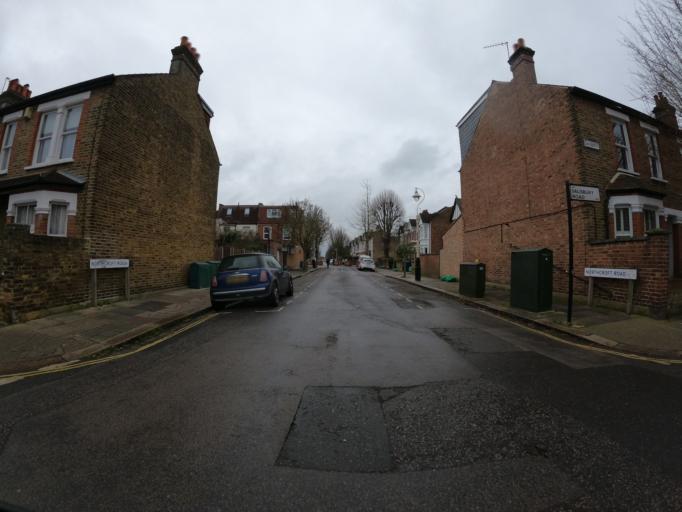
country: GB
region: England
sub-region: Greater London
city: Ealing
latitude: 51.5035
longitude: -0.3210
